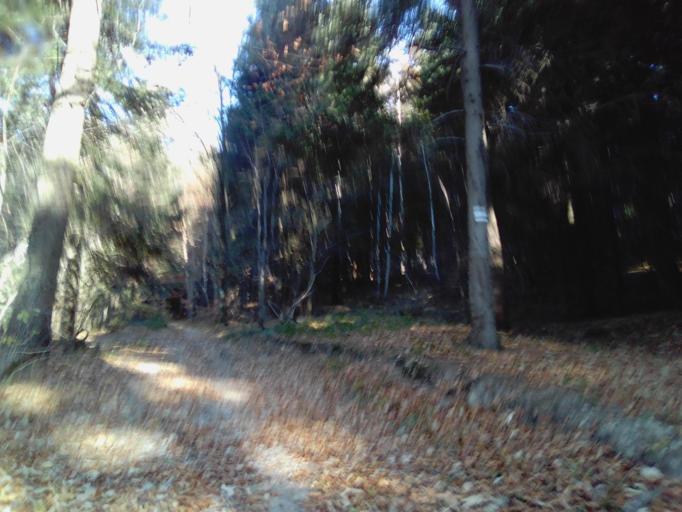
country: PL
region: Subcarpathian Voivodeship
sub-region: Powiat strzyzowski
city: Wysoka Strzyzowska
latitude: 49.8011
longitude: 21.7263
